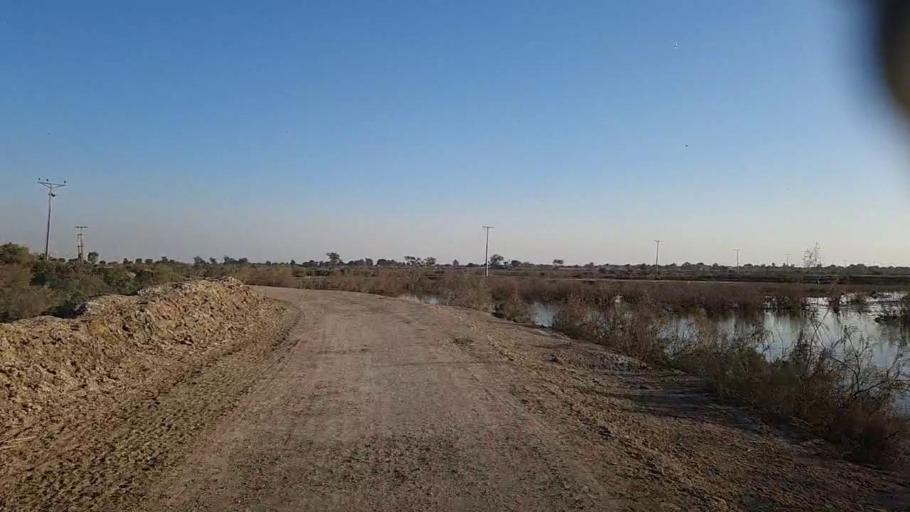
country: PK
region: Sindh
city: Khairpur
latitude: 27.8890
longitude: 69.7077
